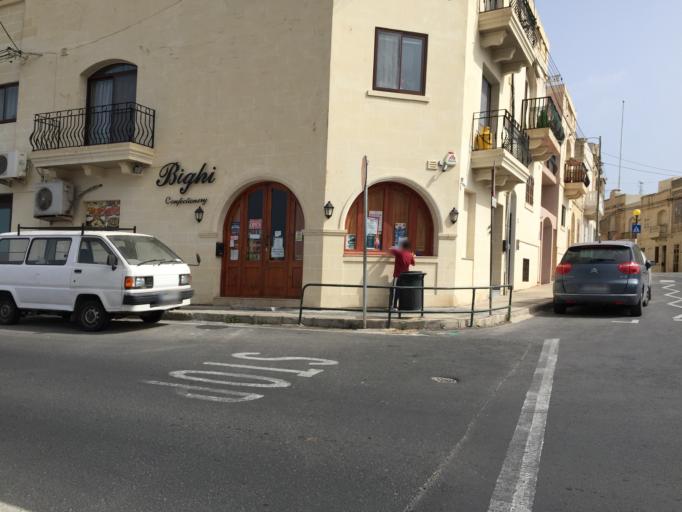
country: MT
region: Bormla
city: Cospicua
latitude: 35.8914
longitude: 14.5268
